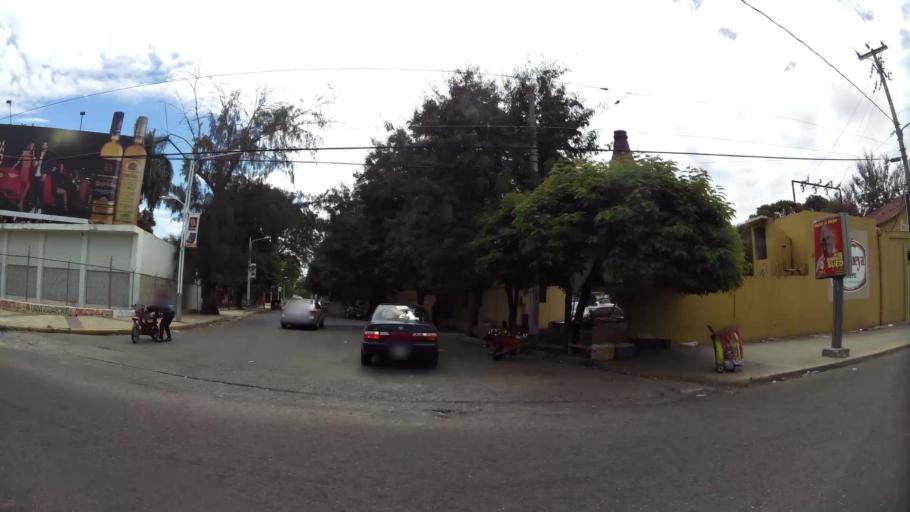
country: DO
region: Santiago
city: Santiago de los Caballeros
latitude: 19.4649
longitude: -70.7109
